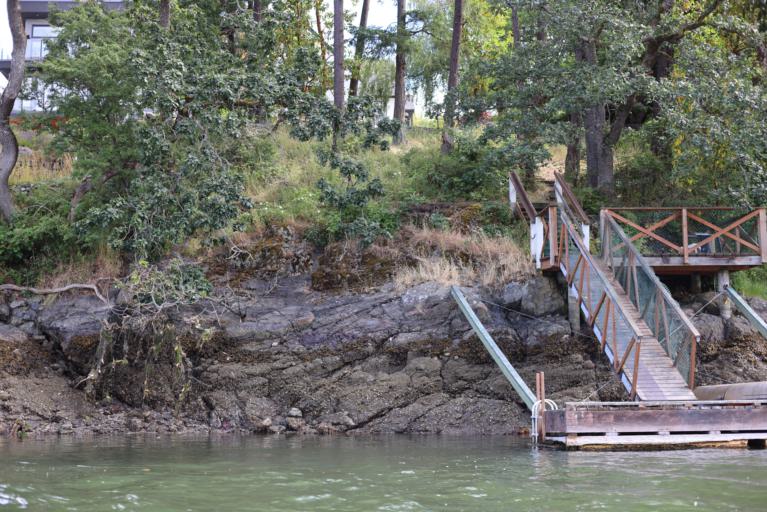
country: CA
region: British Columbia
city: Victoria
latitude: 48.4419
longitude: -123.3906
